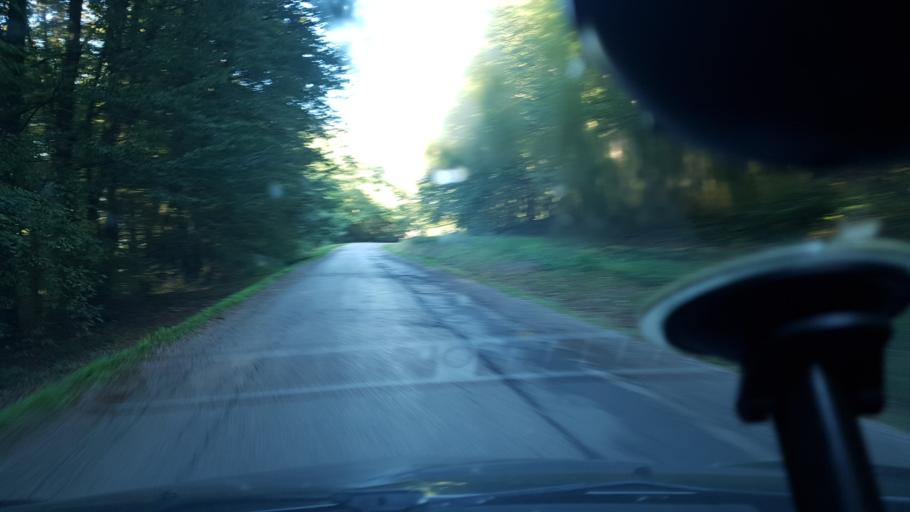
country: HR
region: Bjelovarsko-Bilogorska
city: Bjelovar
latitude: 45.9308
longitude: 16.8675
